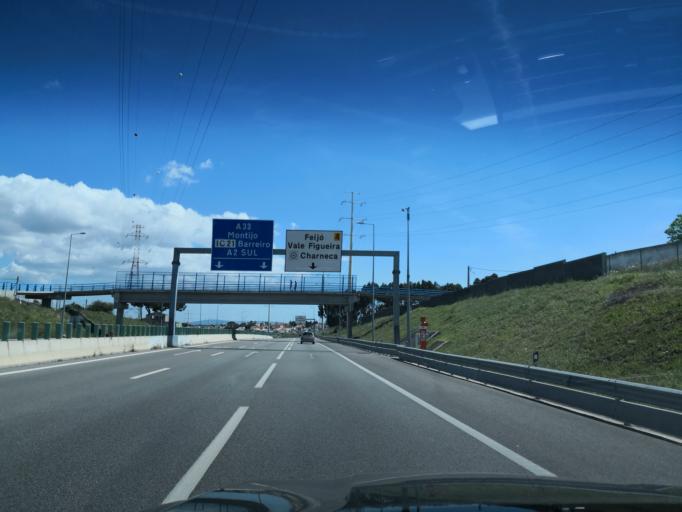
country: PT
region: Setubal
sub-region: Almada
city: Charneca
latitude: 38.6276
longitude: -9.1931
